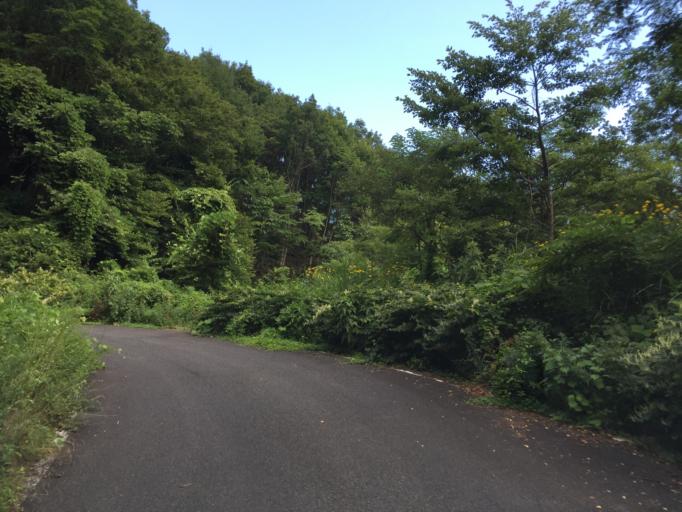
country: JP
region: Fukushima
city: Inawashiro
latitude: 37.4219
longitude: 140.0654
